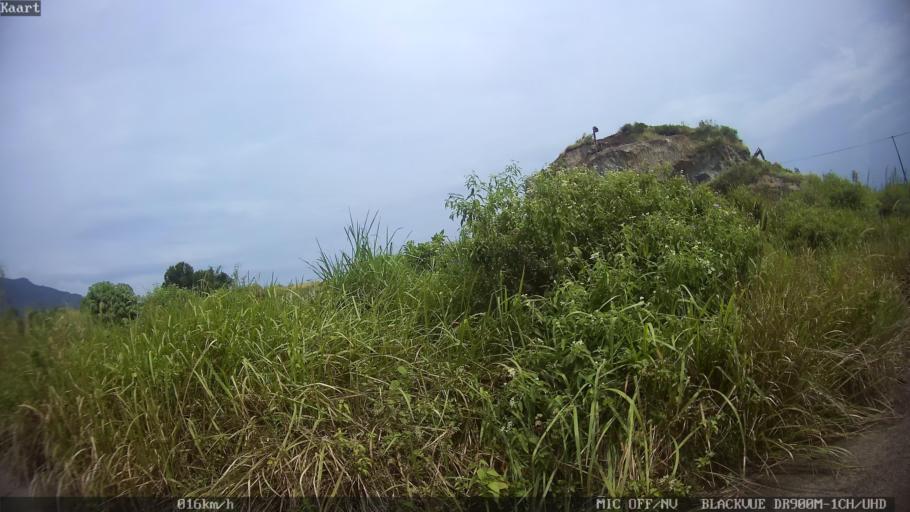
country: ID
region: Lampung
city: Bandarlampung
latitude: -5.4135
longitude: 105.1968
